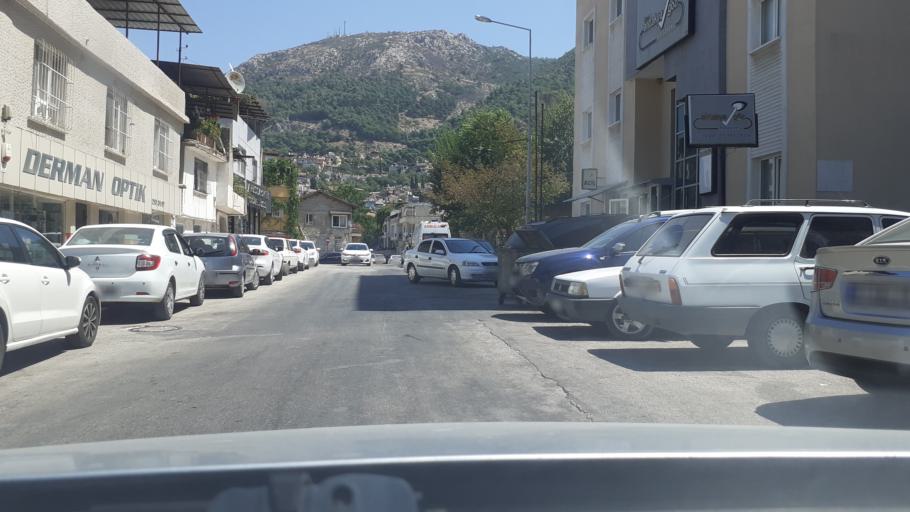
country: TR
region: Hatay
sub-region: Antakya Ilcesi
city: Antakya
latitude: 36.1969
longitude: 36.1638
